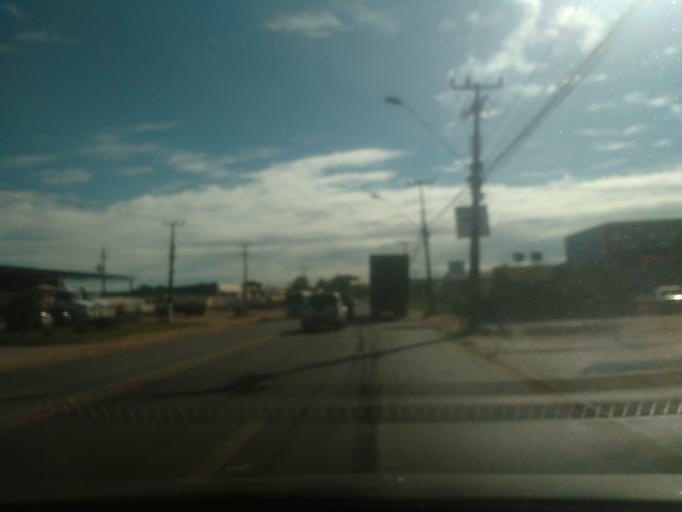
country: BR
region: Alagoas
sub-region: Satuba
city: Satuba
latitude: -9.5606
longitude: -35.7666
